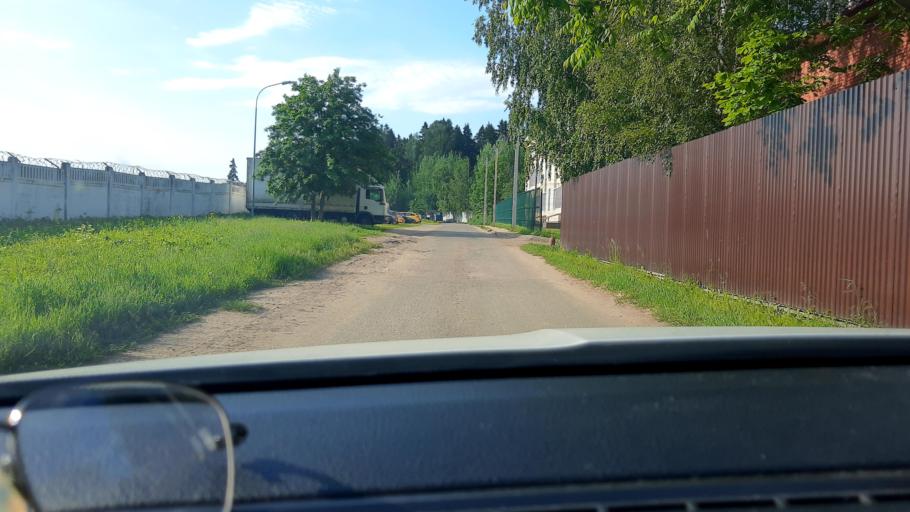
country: RU
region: Moscow
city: Novo-Peredelkino
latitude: 55.6672
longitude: 37.3228
